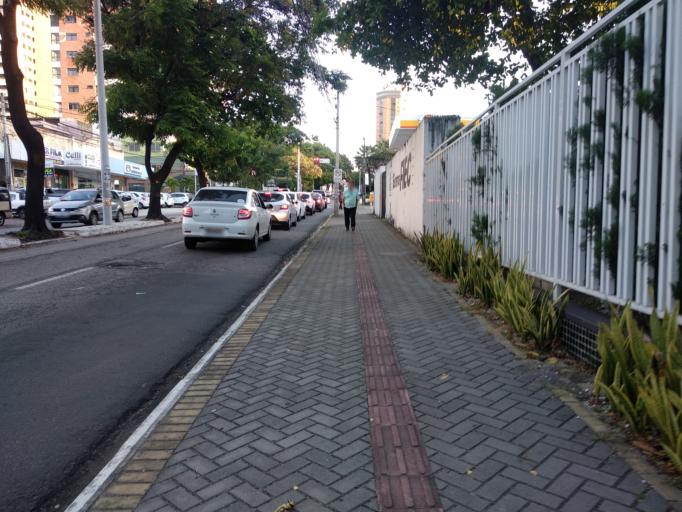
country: BR
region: Ceara
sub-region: Fortaleza
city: Fortaleza
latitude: -3.7409
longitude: -38.5087
